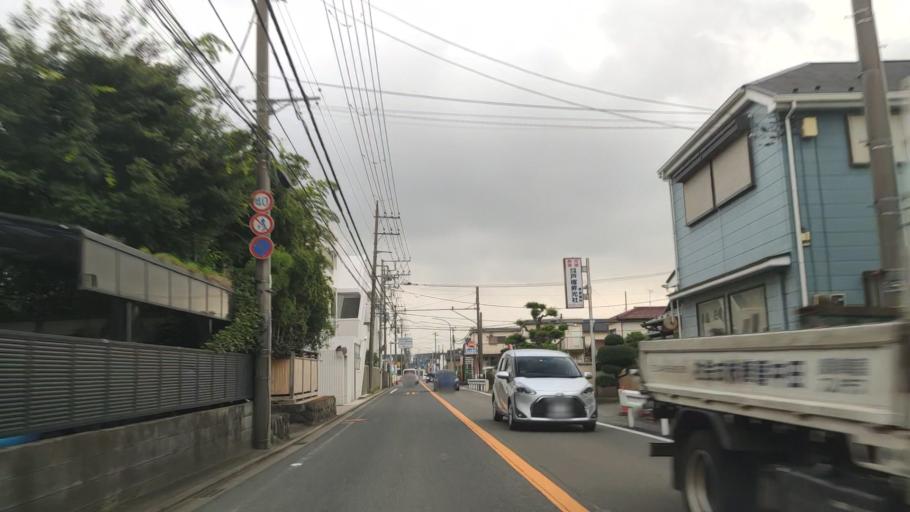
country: JP
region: Kanagawa
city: Minami-rinkan
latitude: 35.4184
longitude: 139.5003
